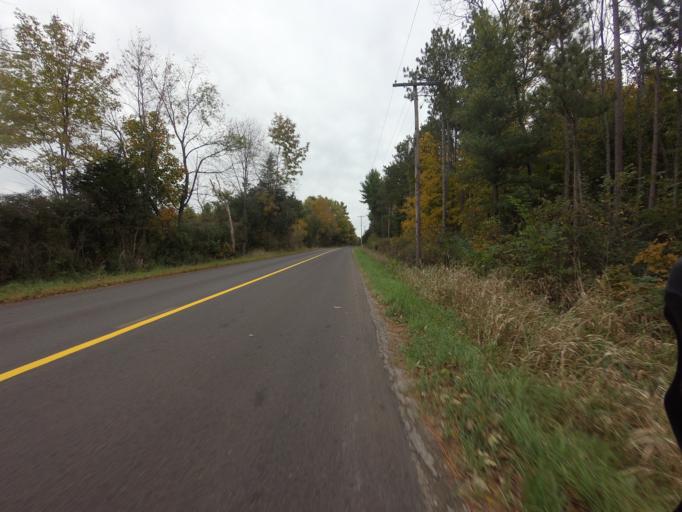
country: CA
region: Ontario
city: Gananoque
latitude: 44.5803
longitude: -76.0783
